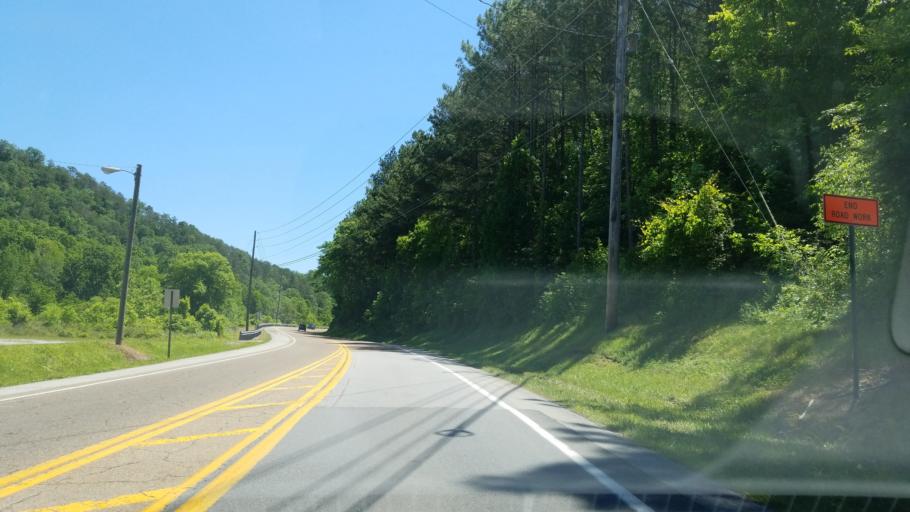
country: US
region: Tennessee
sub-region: Hamilton County
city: Collegedale
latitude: 35.0579
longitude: -85.0620
